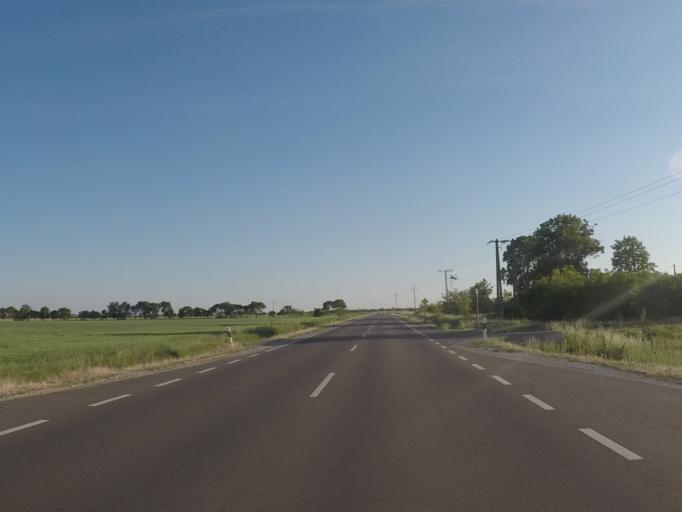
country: HU
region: Heves
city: Besenyotelek
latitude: 47.6871
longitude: 20.3892
